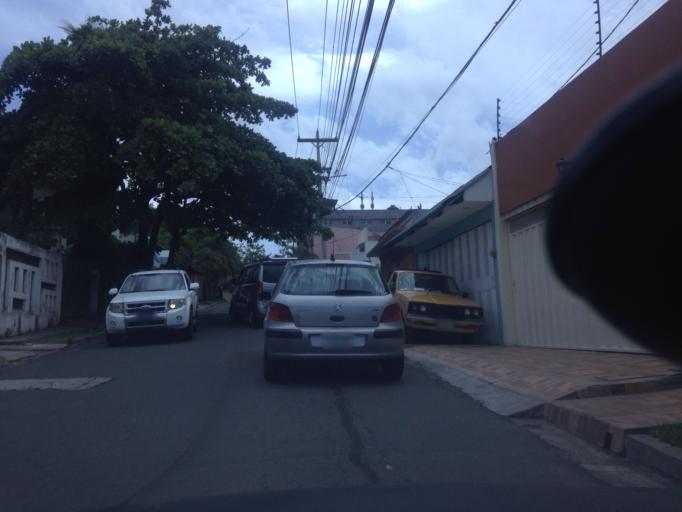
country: HN
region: Francisco Morazan
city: Tegucigalpa
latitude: 14.0793
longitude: -87.1978
